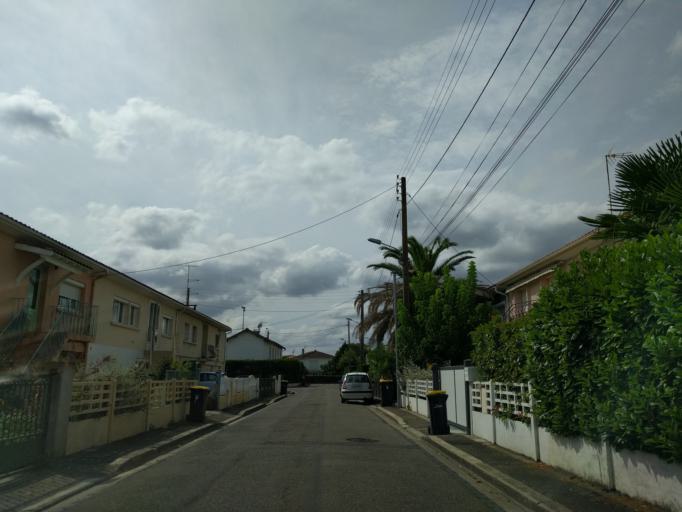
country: FR
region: Aquitaine
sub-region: Departement du Lot-et-Garonne
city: Agen
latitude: 44.1911
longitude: 0.6265
